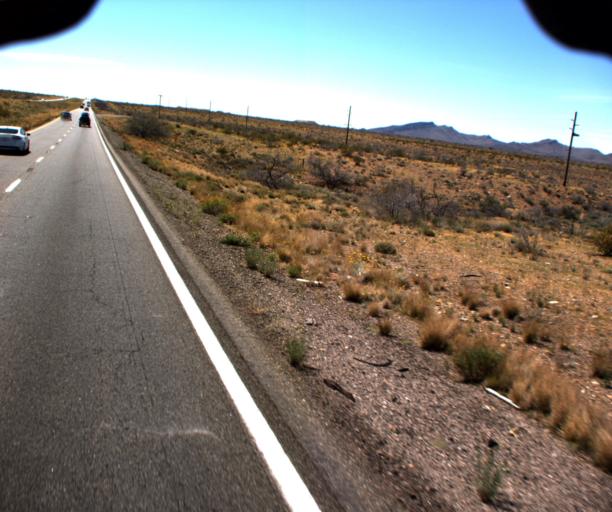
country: US
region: Arizona
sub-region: Mohave County
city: Dolan Springs
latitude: 35.4356
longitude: -114.2876
